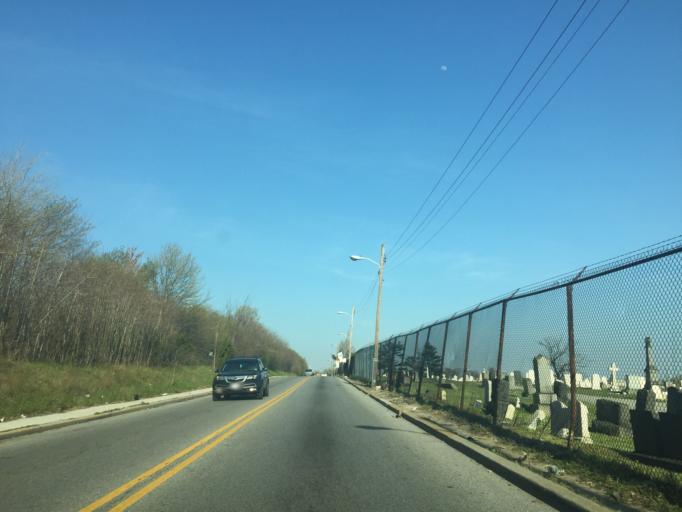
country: US
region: Maryland
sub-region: City of Baltimore
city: Baltimore
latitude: 39.3142
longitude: -76.5771
